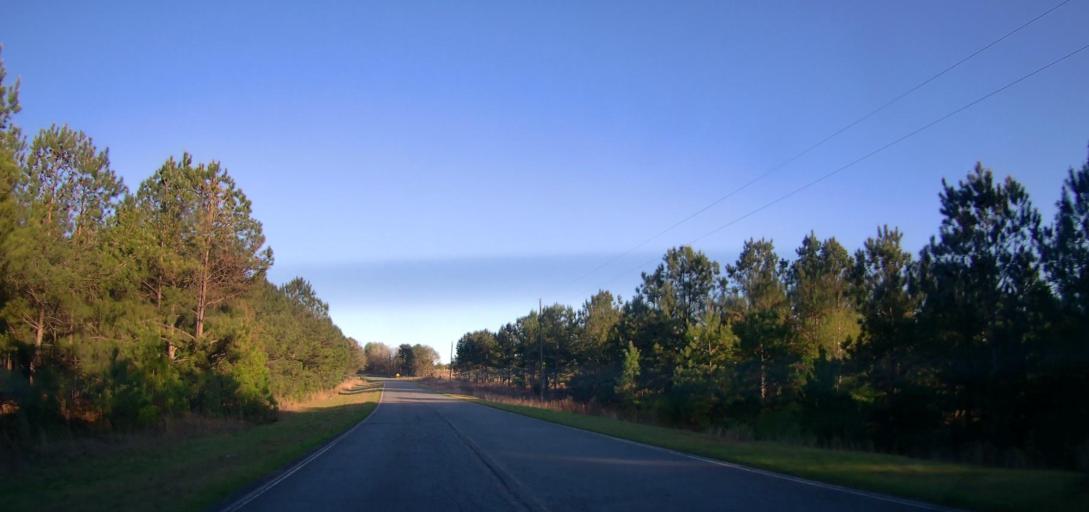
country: US
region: Georgia
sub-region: Wilkinson County
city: Gordon
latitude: 32.8723
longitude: -83.2455
